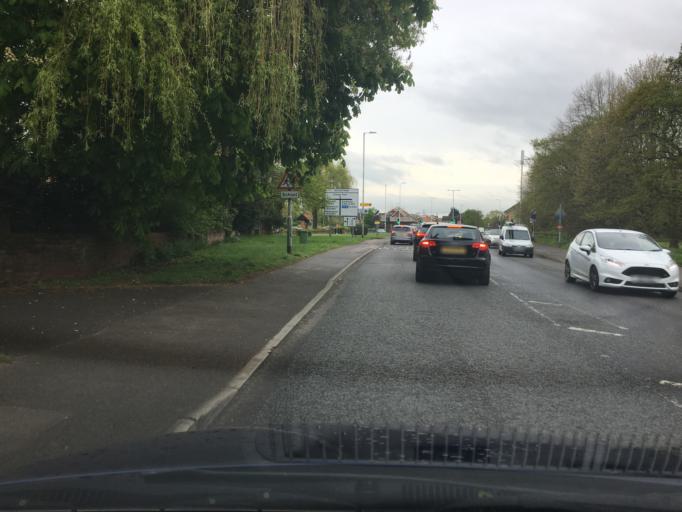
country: GB
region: England
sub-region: Bracknell Forest
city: Sandhurst
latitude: 51.3459
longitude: -0.7874
